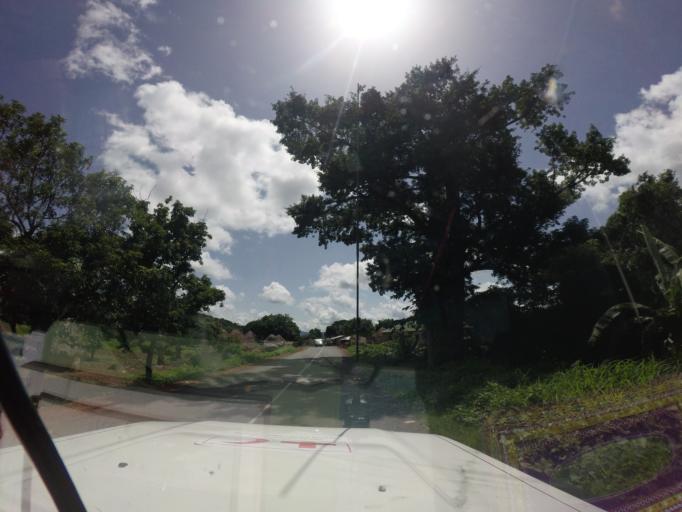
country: GN
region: Mamou
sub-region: Mamou Prefecture
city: Mamou
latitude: 10.1747
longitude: -11.7950
